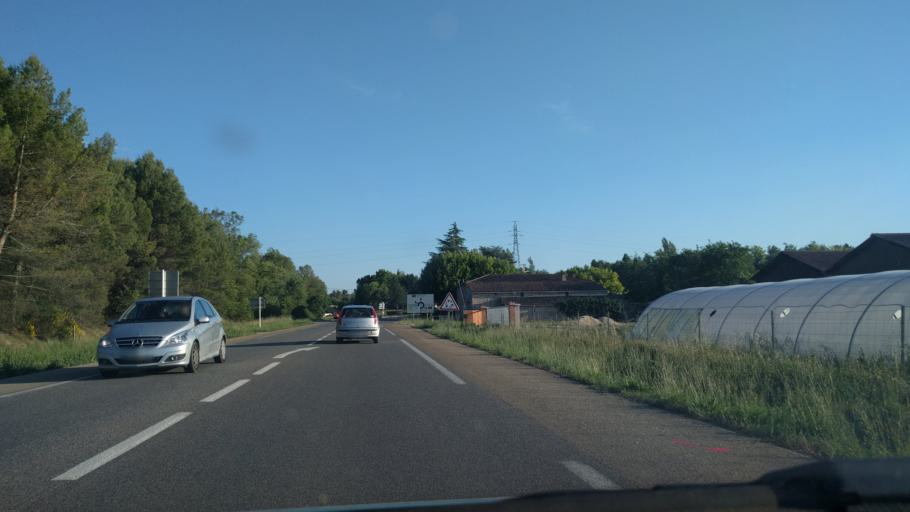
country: FR
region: Provence-Alpes-Cote d'Azur
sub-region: Departement des Bouches-du-Rhone
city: Meyrargues
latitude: 43.6495
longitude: 5.4922
